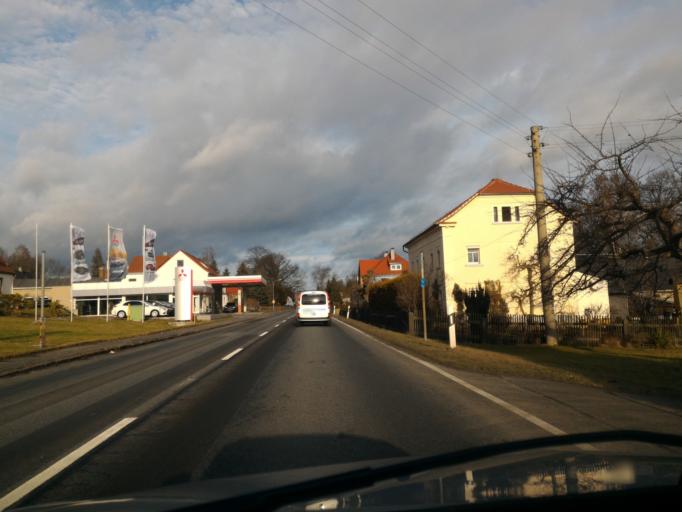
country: DE
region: Saxony
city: Friedersdorf
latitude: 51.0256
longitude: 14.5587
